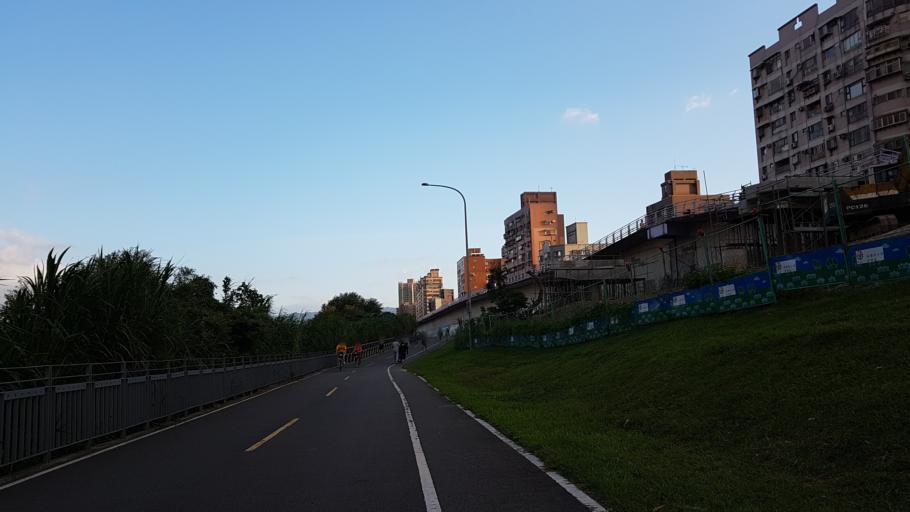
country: TW
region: Taipei
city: Taipei
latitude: 25.0164
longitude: 121.5205
